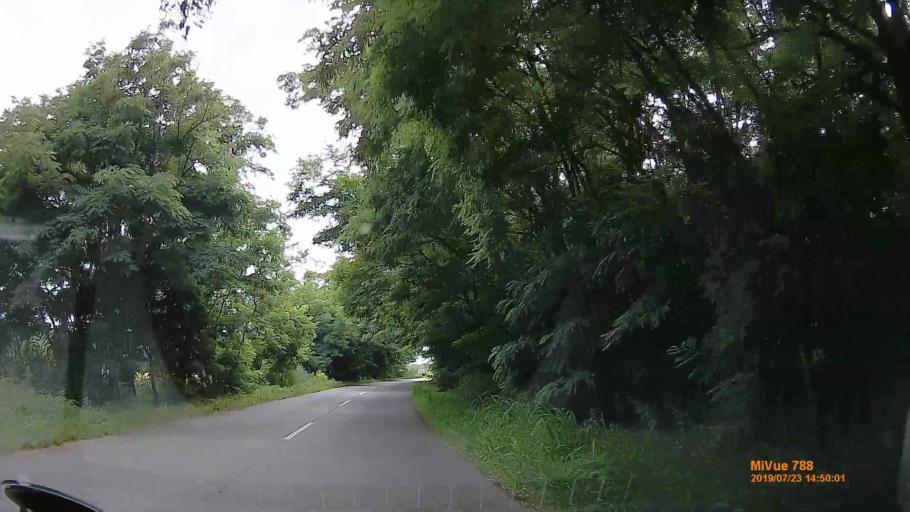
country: HU
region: Szabolcs-Szatmar-Bereg
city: Kalmanhaza
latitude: 47.8914
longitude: 21.6590
